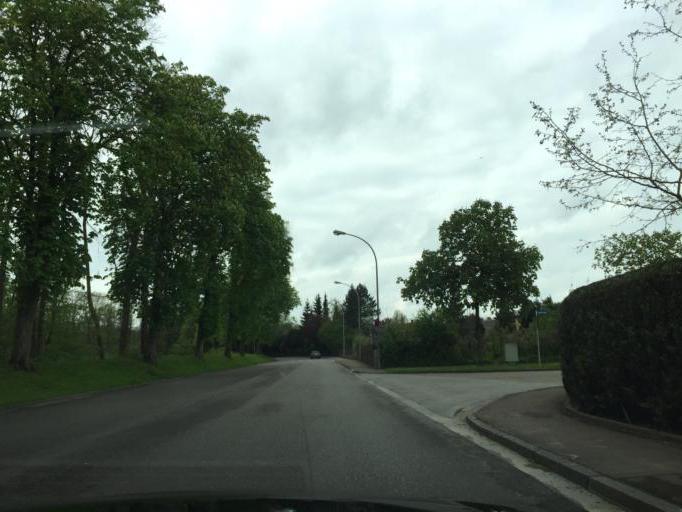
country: DE
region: Bavaria
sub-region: Swabia
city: Dillingen an der Donau
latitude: 48.5716
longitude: 10.4933
